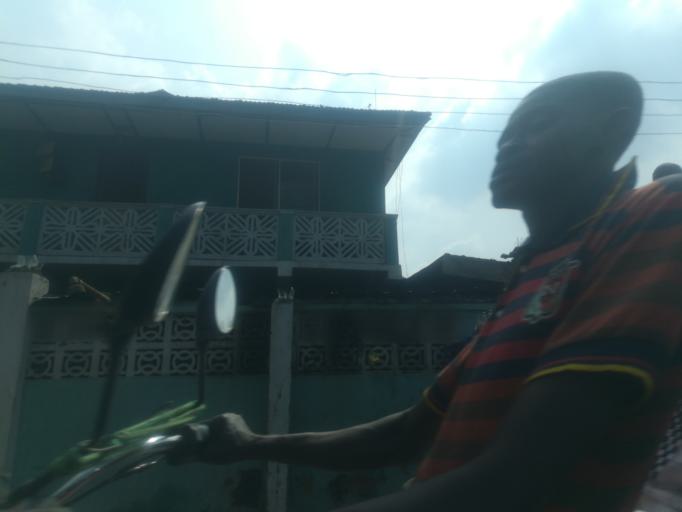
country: NG
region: Oyo
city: Ibadan
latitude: 7.3941
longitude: 3.9076
